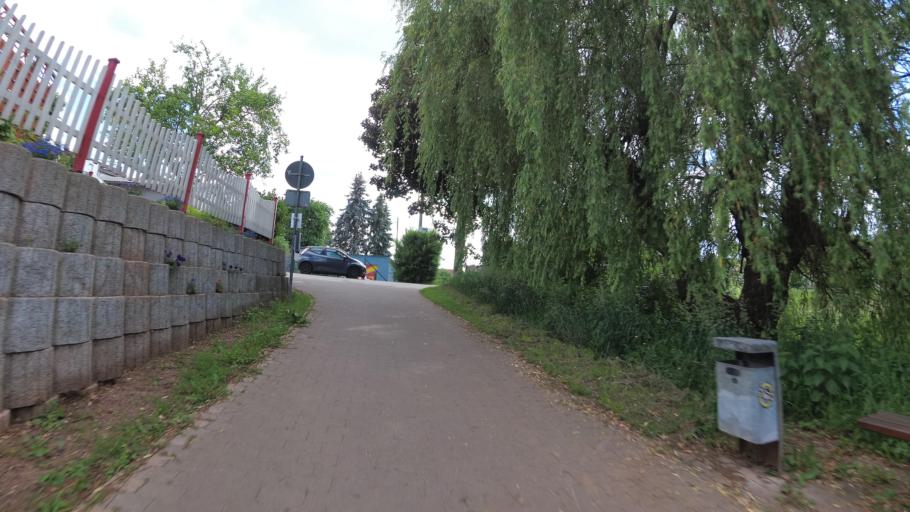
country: DE
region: Saarland
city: Puttlingen
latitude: 49.3033
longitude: 6.8984
